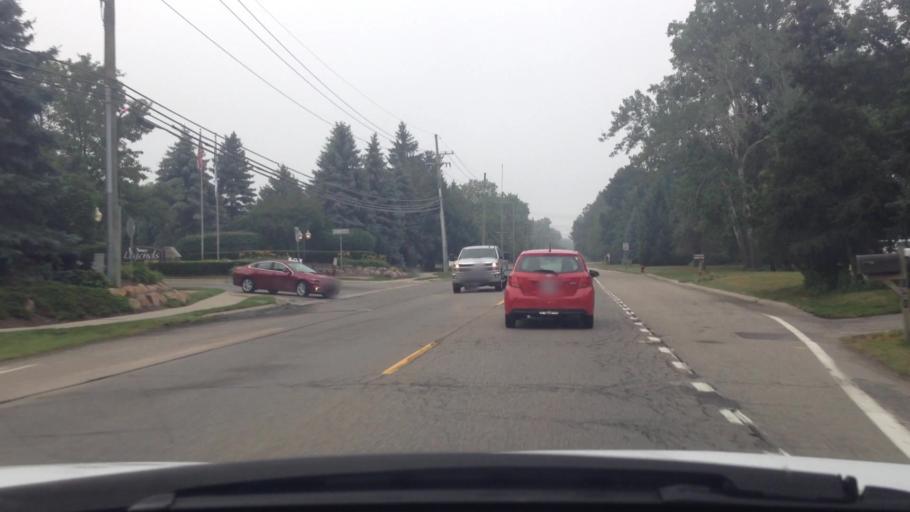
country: US
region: Michigan
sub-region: Oakland County
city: Waterford
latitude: 42.7134
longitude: -83.3490
